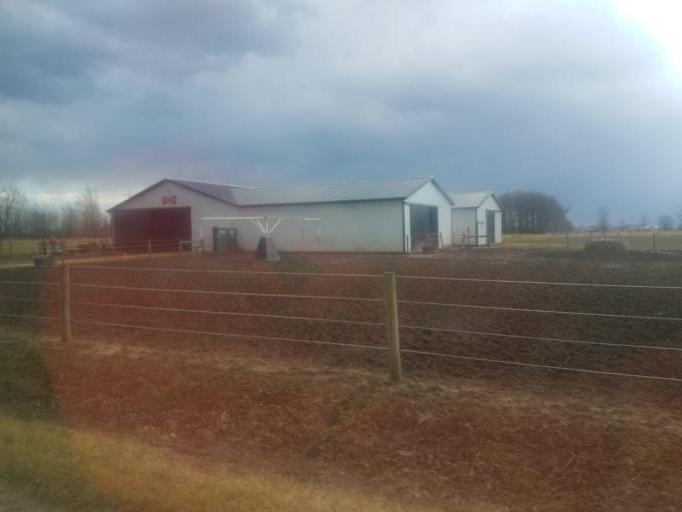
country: US
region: Ohio
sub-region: Marion County
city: Prospect
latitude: 40.4706
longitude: -83.1156
